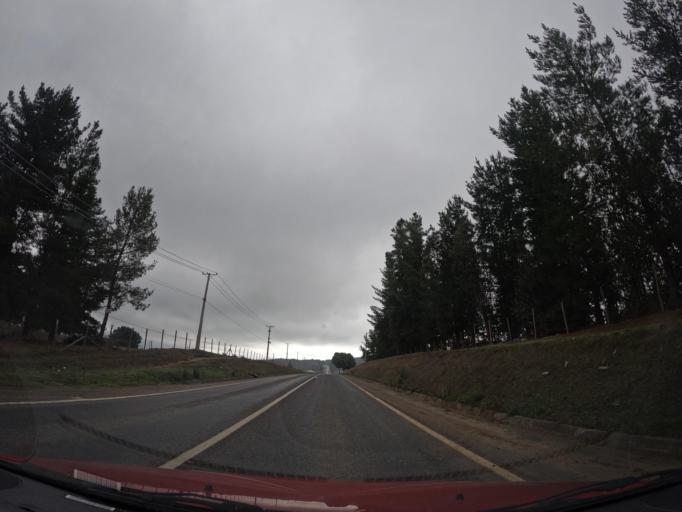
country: CL
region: Maule
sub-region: Provincia de Cauquenes
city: Cauquenes
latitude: -36.2474
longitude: -72.5484
